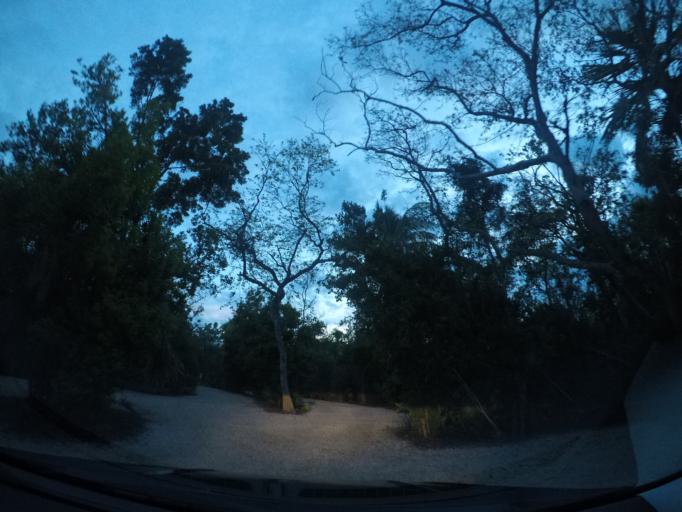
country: US
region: Florida
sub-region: Monroe County
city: Marathon
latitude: 24.7168
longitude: -81.0755
